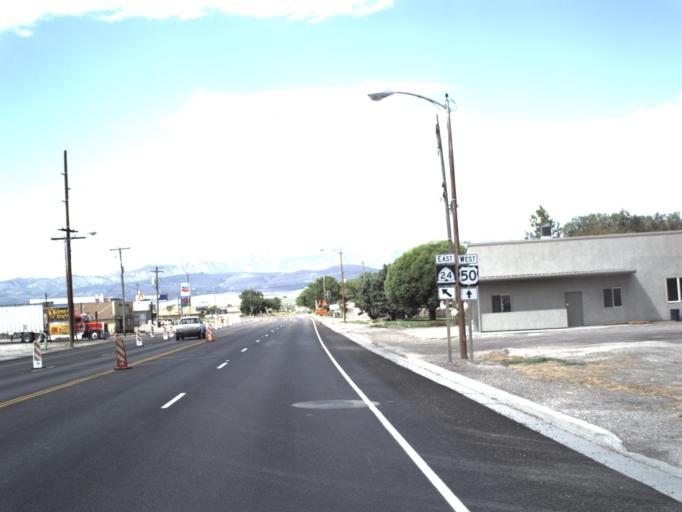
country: US
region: Utah
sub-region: Sevier County
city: Salina
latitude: 38.9574
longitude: -111.8667
